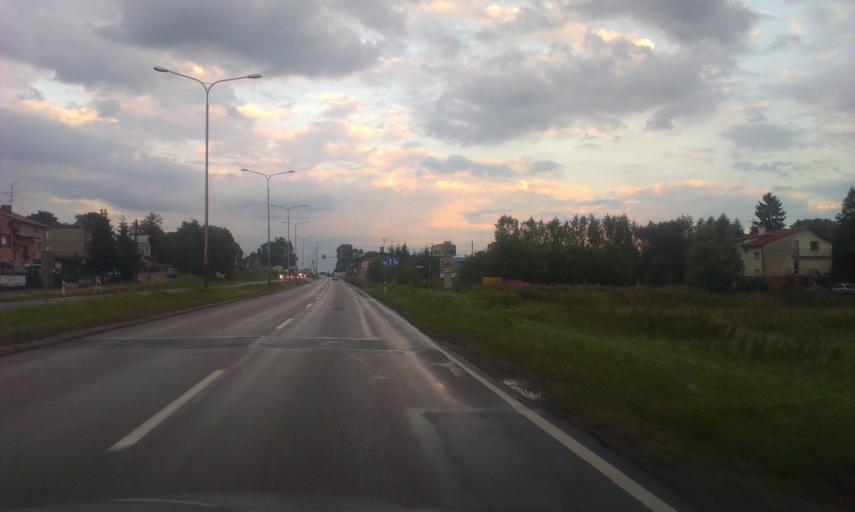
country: PL
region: West Pomeranian Voivodeship
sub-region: Koszalin
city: Koszalin
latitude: 54.1650
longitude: 16.2161
